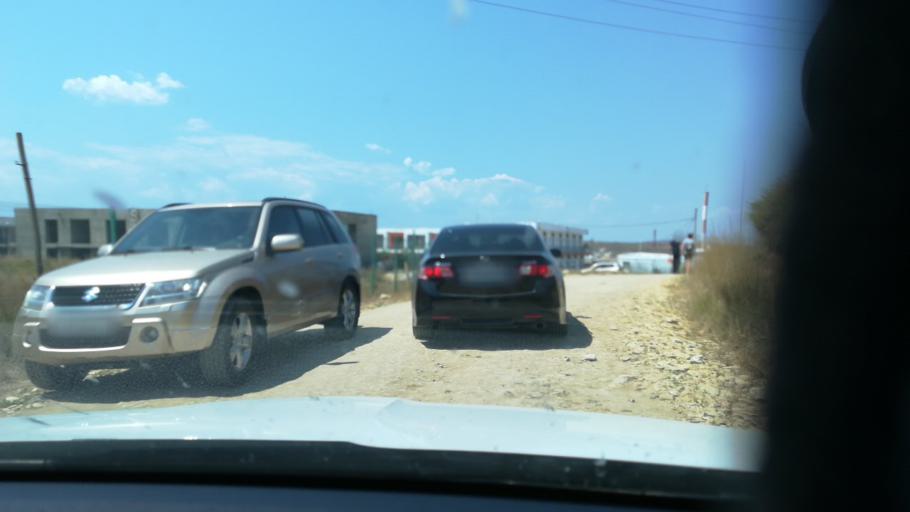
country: RU
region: Krasnodarskiy
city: Vyshestebliyevskaya
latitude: 45.1122
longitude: 36.8748
